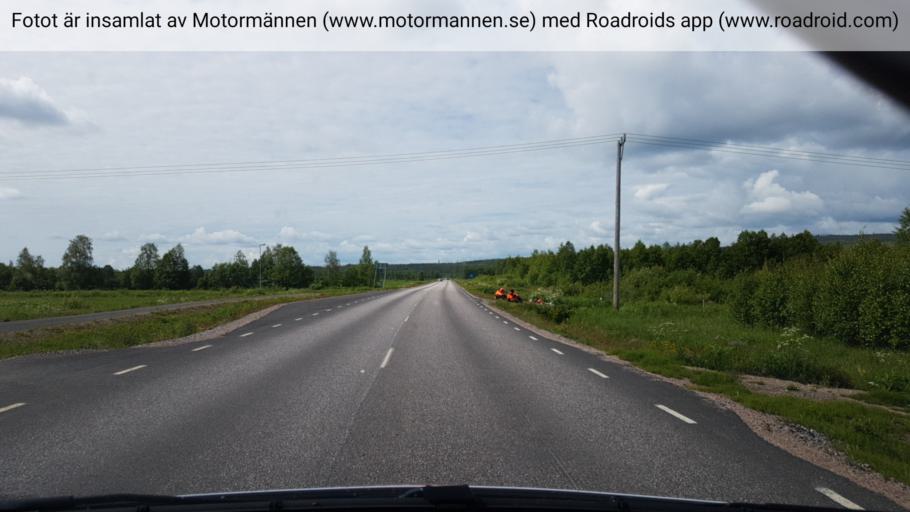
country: SE
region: Norrbotten
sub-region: Overtornea Kommun
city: OEvertornea
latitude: 66.5528
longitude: 23.8088
